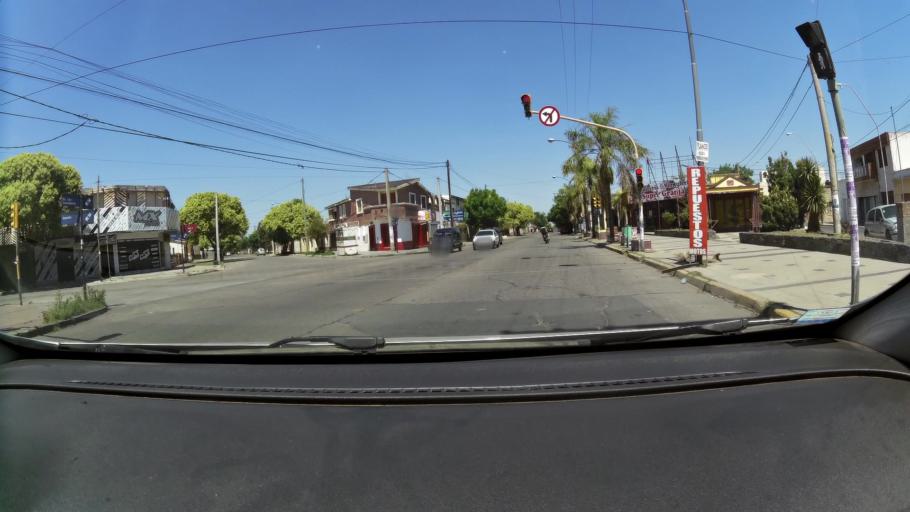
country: AR
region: Cordoba
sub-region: Departamento de Capital
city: Cordoba
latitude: -31.3782
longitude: -64.2045
